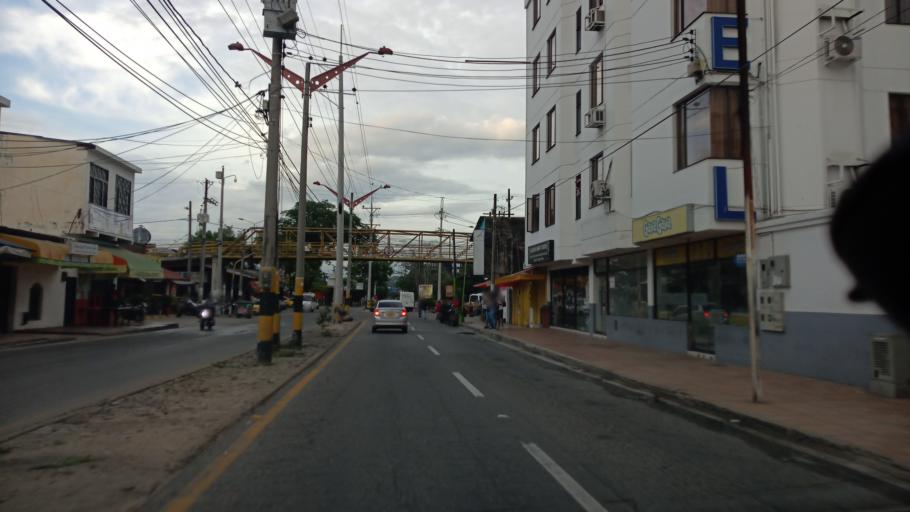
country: CO
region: Tolima
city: Melgar
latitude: 4.2057
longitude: -74.6432
